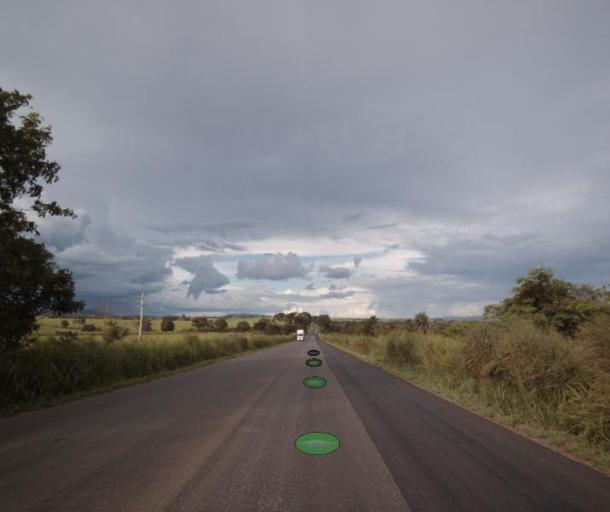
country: BR
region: Goias
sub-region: Ceres
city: Ceres
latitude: -15.1383
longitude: -49.5229
